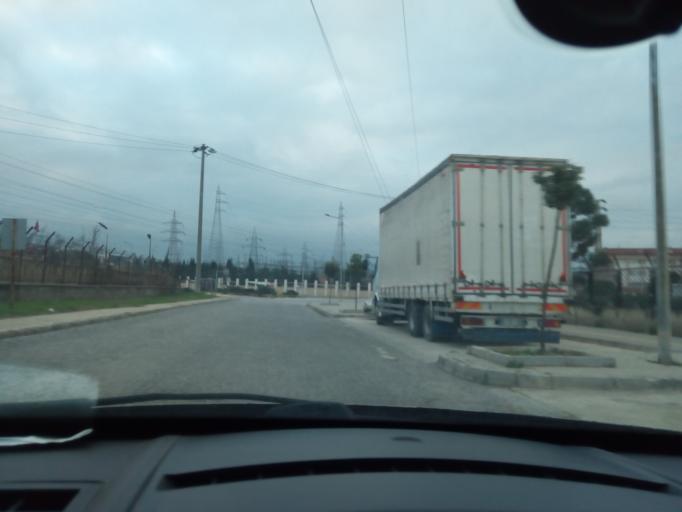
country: TR
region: Bursa
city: Niluefer
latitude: 40.2359
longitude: 28.9678
